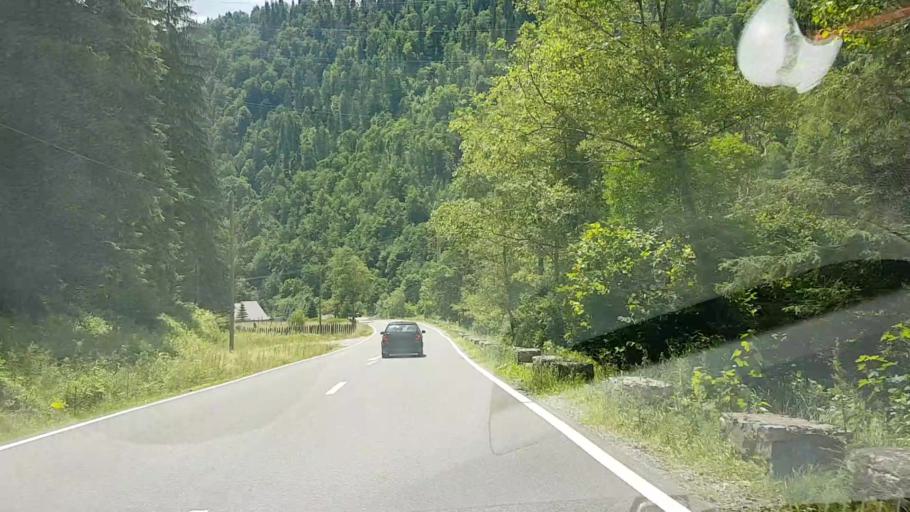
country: RO
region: Suceava
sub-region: Comuna Brosteni
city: Brosteni
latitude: 47.2767
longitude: 25.6490
